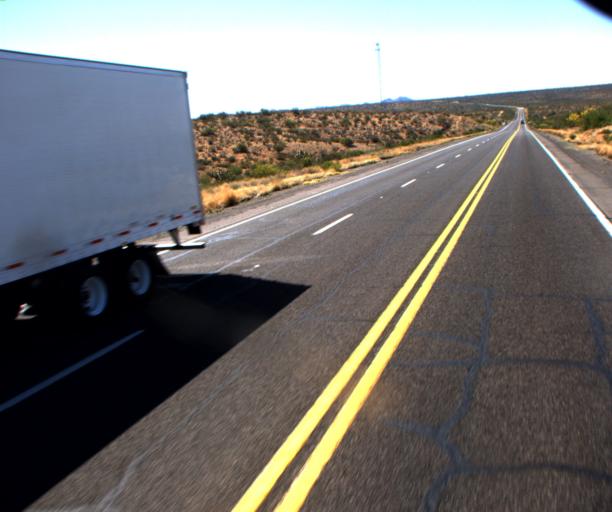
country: US
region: Arizona
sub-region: Yavapai County
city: Congress
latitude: 34.2199
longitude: -113.0685
